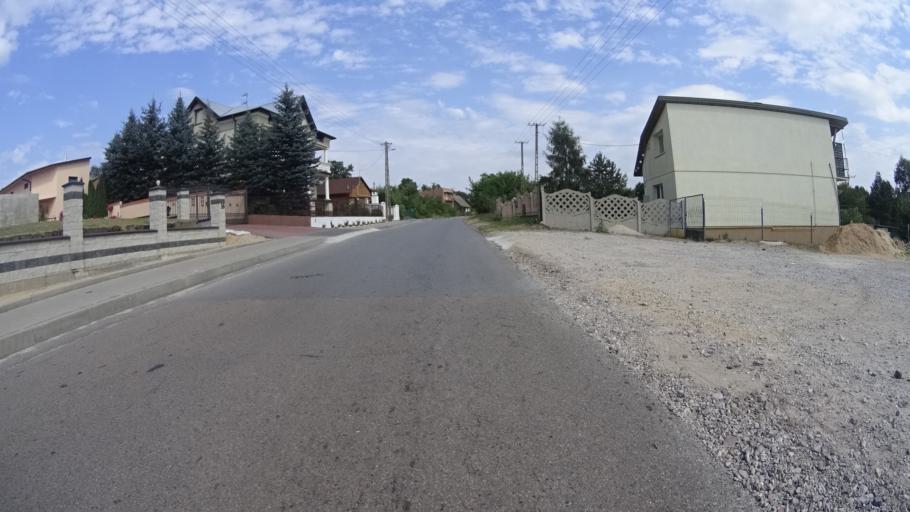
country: PL
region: Masovian Voivodeship
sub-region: Powiat bialobrzeski
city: Wysmierzyce
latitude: 51.6527
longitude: 20.8077
